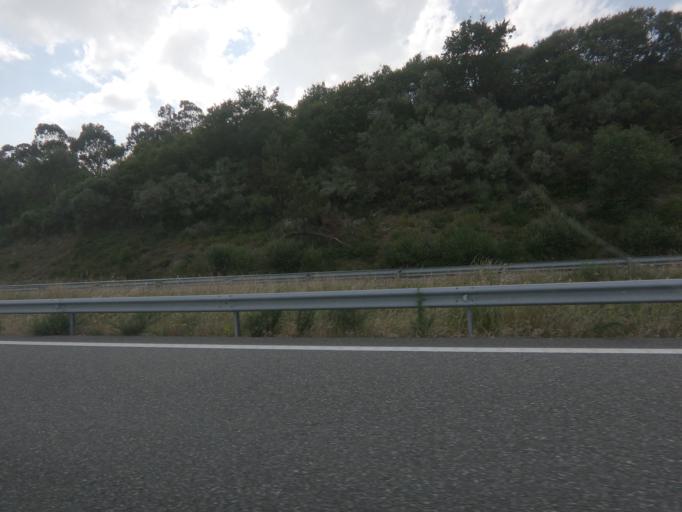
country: ES
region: Galicia
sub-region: Provincia de Ourense
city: Melon
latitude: 42.2381
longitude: -8.2290
